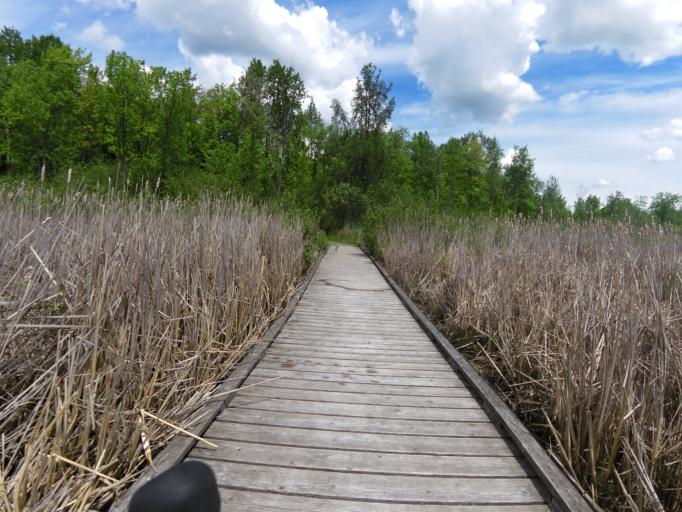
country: CA
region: Ontario
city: Ottawa
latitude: 45.3930
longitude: -75.5092
